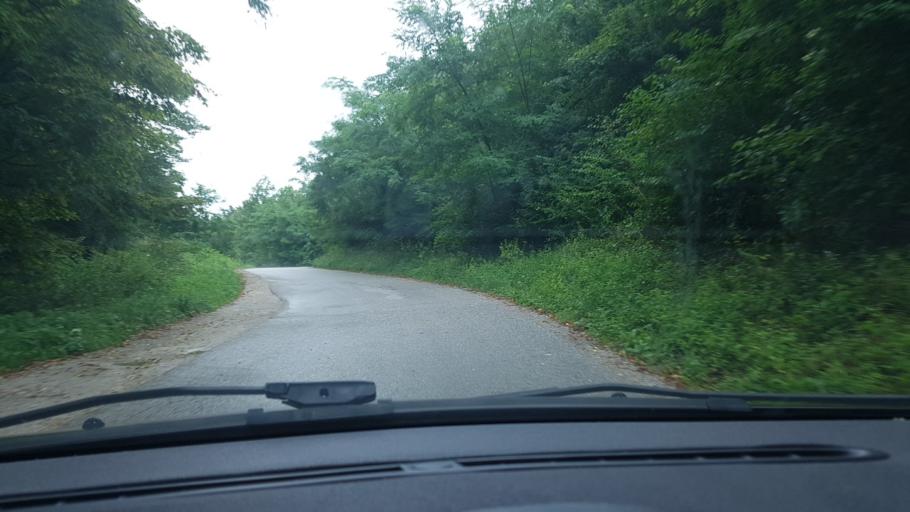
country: HR
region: Karlovacka
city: Ozalj
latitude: 45.6044
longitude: 15.5379
